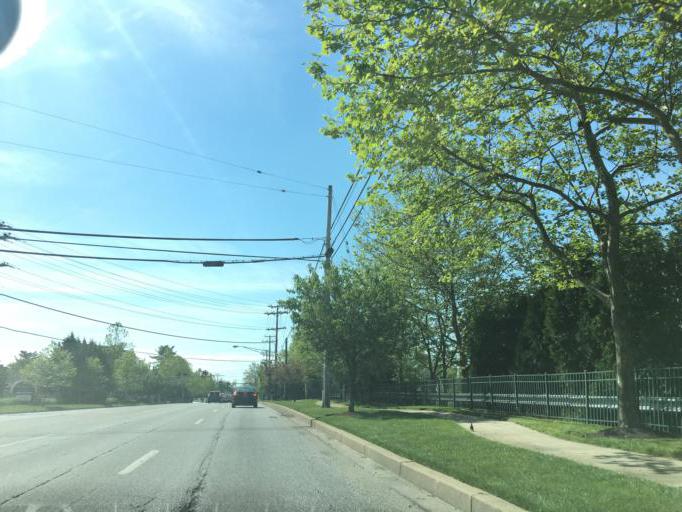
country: US
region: Maryland
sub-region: Baltimore County
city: Garrison
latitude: 39.3961
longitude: -76.7476
